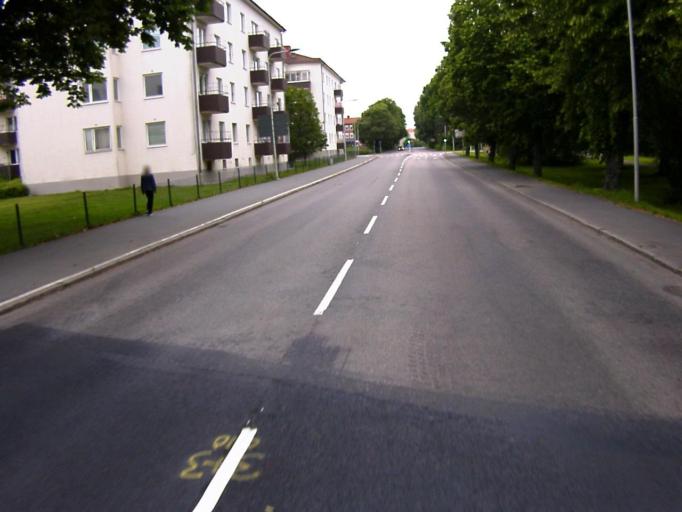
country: SE
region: Skane
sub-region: Kristianstads Kommun
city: Kristianstad
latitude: 56.0313
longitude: 14.1679
